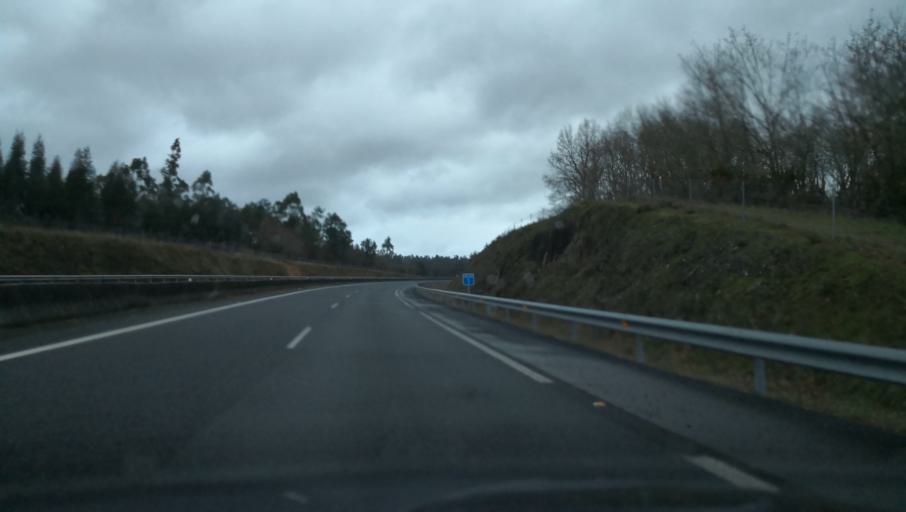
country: ES
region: Galicia
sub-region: Provincia da Coruna
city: Vedra
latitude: 42.8138
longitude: -8.4846
